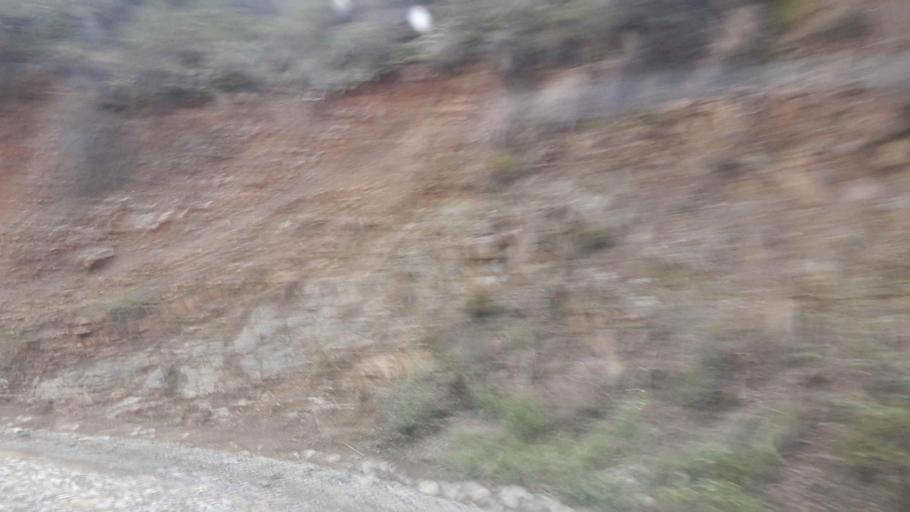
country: BO
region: Cochabamba
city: Cochabamba
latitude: -17.3693
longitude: -66.0619
